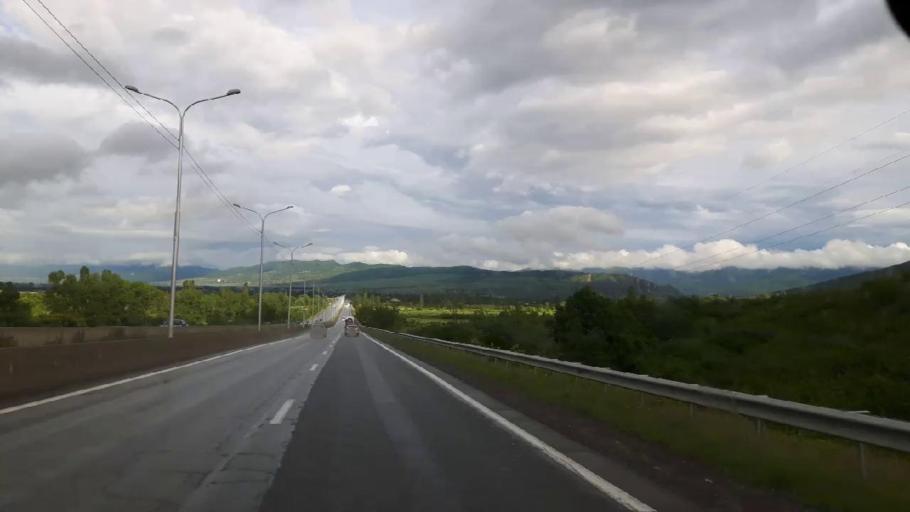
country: GE
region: Shida Kartli
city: Kaspi
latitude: 41.9265
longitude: 44.5354
